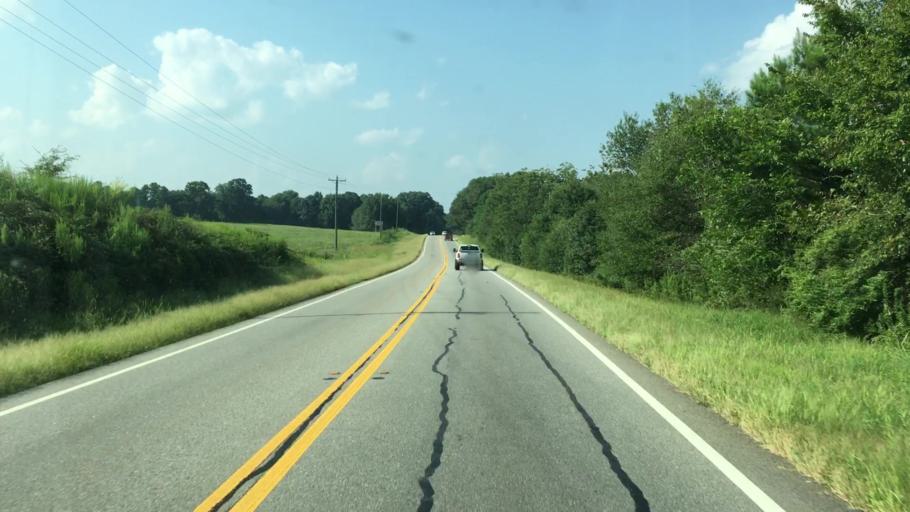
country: US
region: Georgia
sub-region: Walton County
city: Monroe
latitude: 33.8798
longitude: -83.7209
